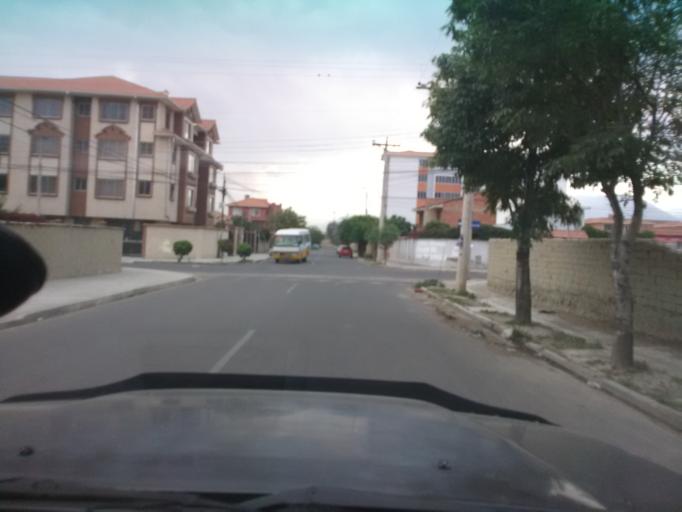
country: BO
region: Cochabamba
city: Cochabamba
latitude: -17.3805
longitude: -66.1834
